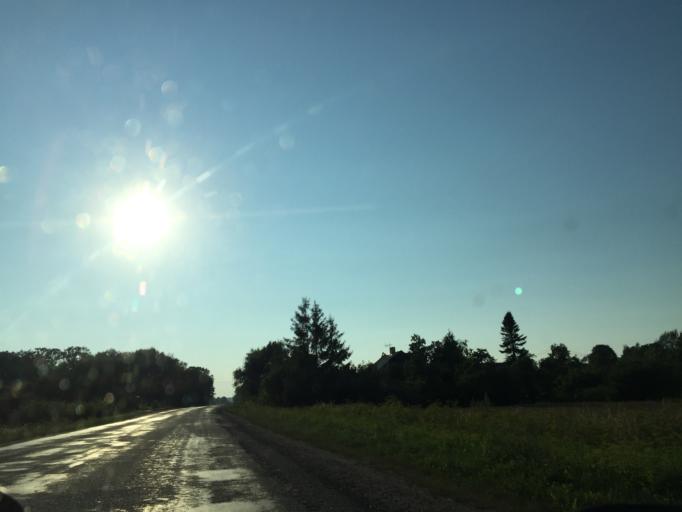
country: LV
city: Tervete
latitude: 56.4414
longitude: 23.4836
